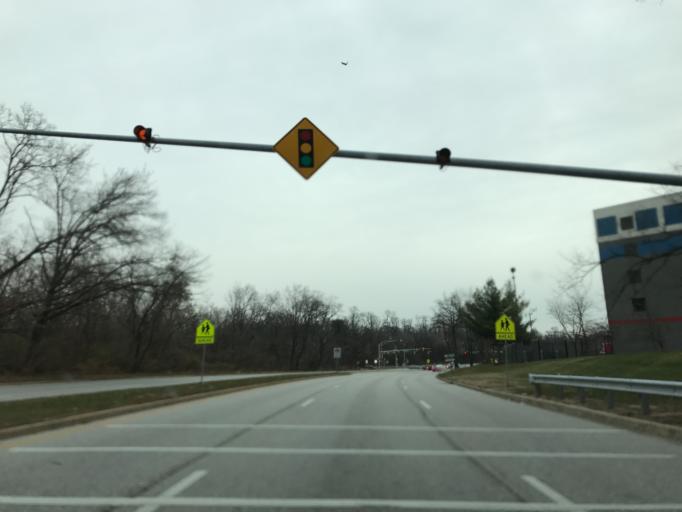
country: US
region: Maryland
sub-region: Baltimore County
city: Parkville
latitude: 39.3721
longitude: -76.5699
